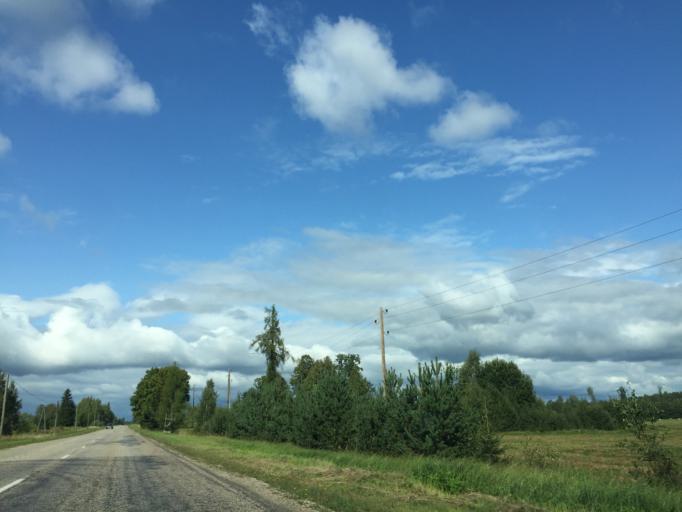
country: LV
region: Pargaujas
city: Stalbe
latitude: 57.4128
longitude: 24.9540
